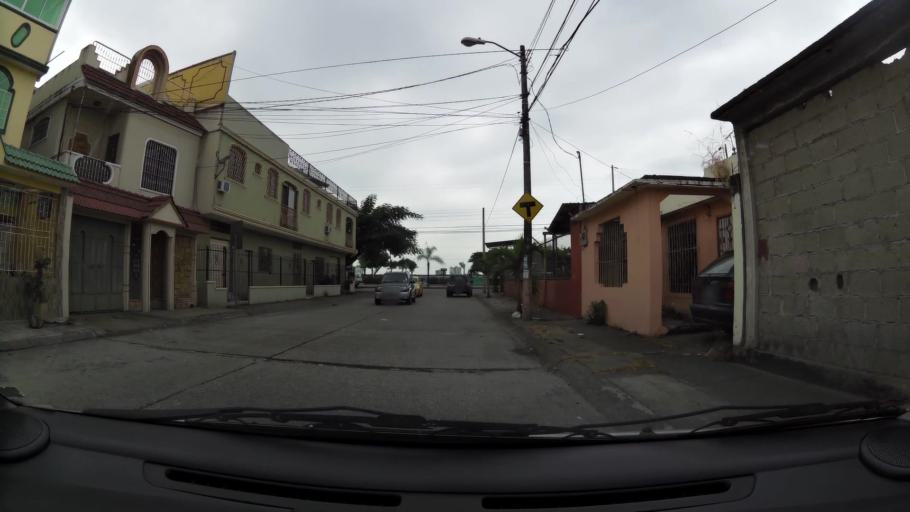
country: EC
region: Guayas
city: Eloy Alfaro
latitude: -2.1201
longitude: -79.8835
